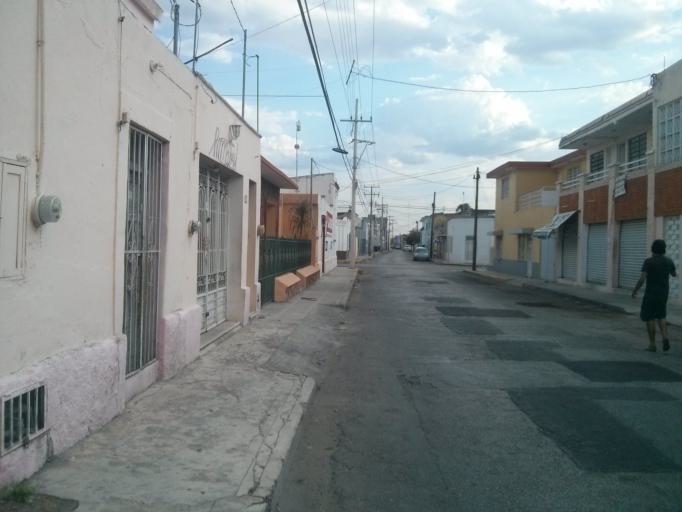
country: MX
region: Yucatan
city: Merida
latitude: 20.9650
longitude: -89.6129
